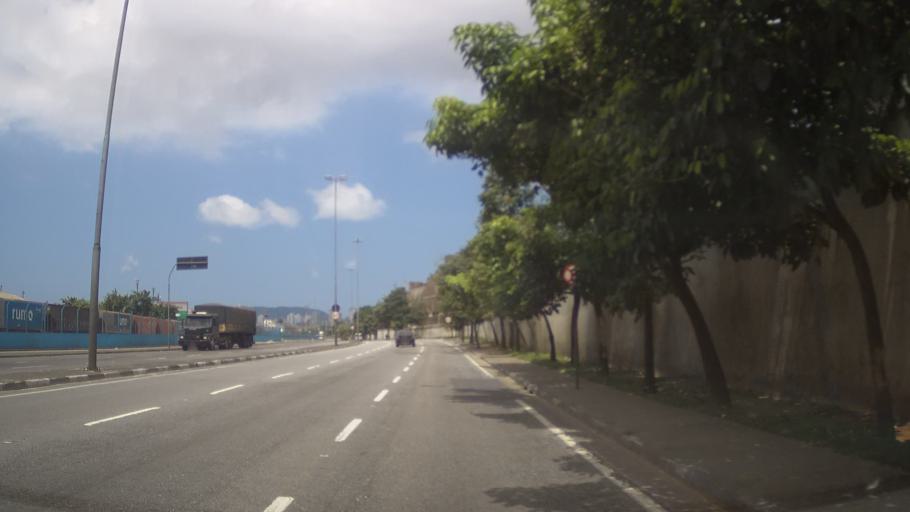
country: BR
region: Sao Paulo
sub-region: Santos
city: Santos
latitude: -23.9431
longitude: -46.3175
